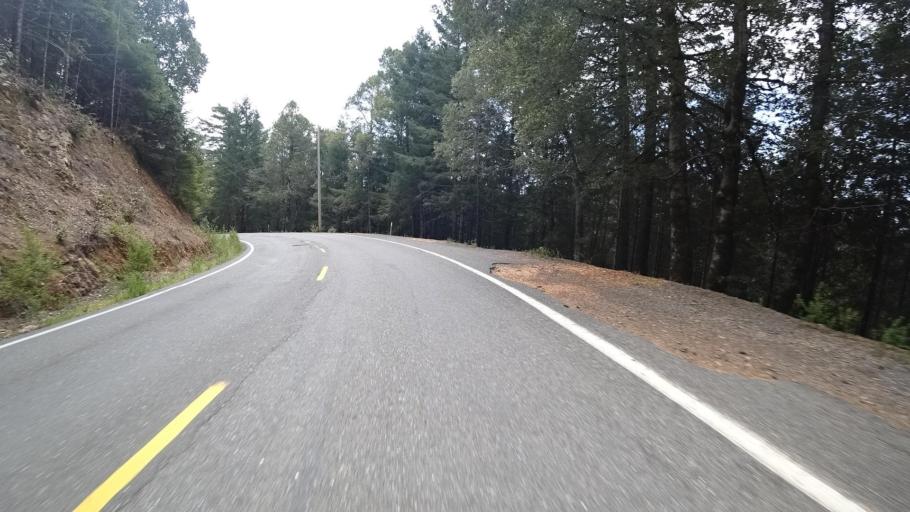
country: US
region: California
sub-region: Humboldt County
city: Redway
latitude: 40.0458
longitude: -124.0216
